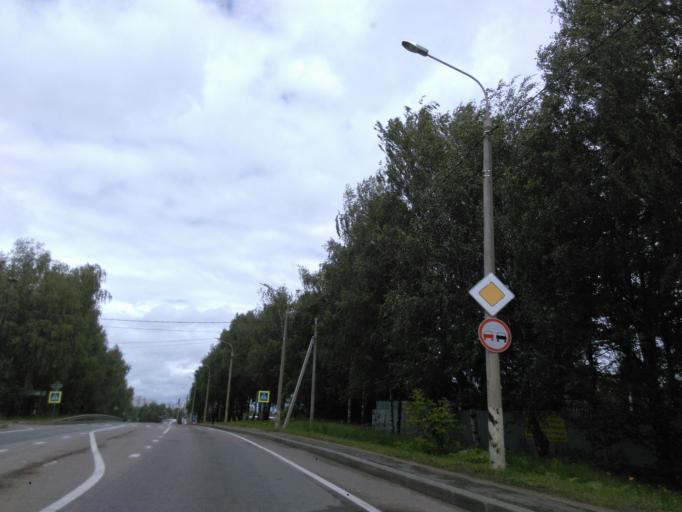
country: RU
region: Moskovskaya
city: Solnechnogorsk
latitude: 56.1826
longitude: 36.9599
